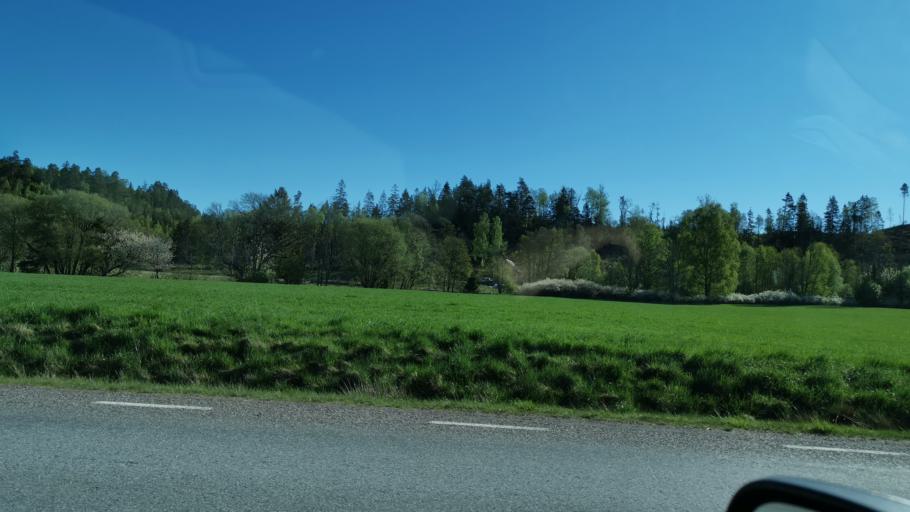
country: SE
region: Vaestra Goetaland
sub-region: Uddevalla Kommun
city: Ljungskile
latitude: 58.2611
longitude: 11.9018
